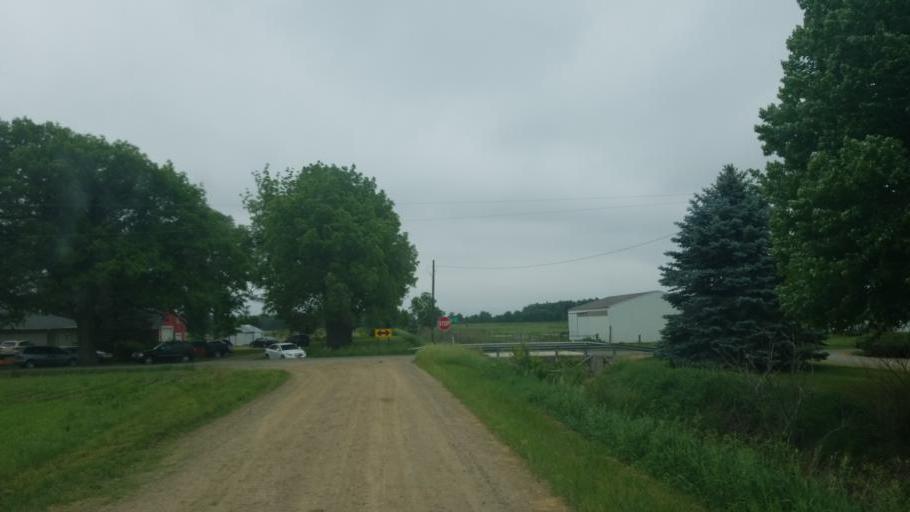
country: US
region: Indiana
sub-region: Elkhart County
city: Nappanee
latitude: 41.4577
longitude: -86.0400
